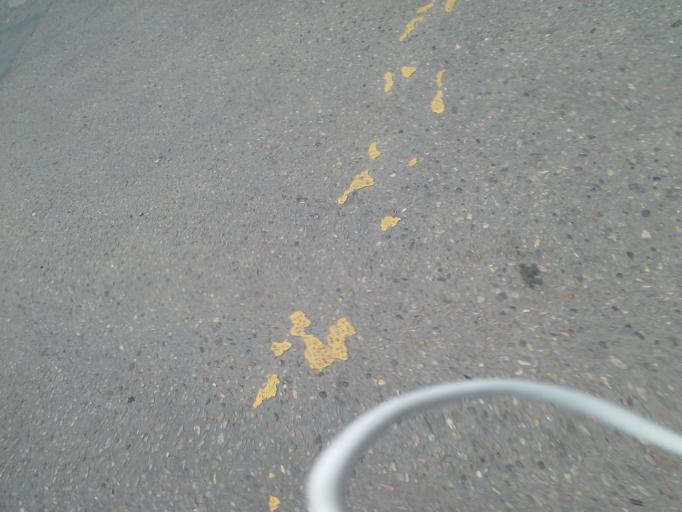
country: CO
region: Bogota D.C.
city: Bogota
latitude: 4.5990
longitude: -74.1447
